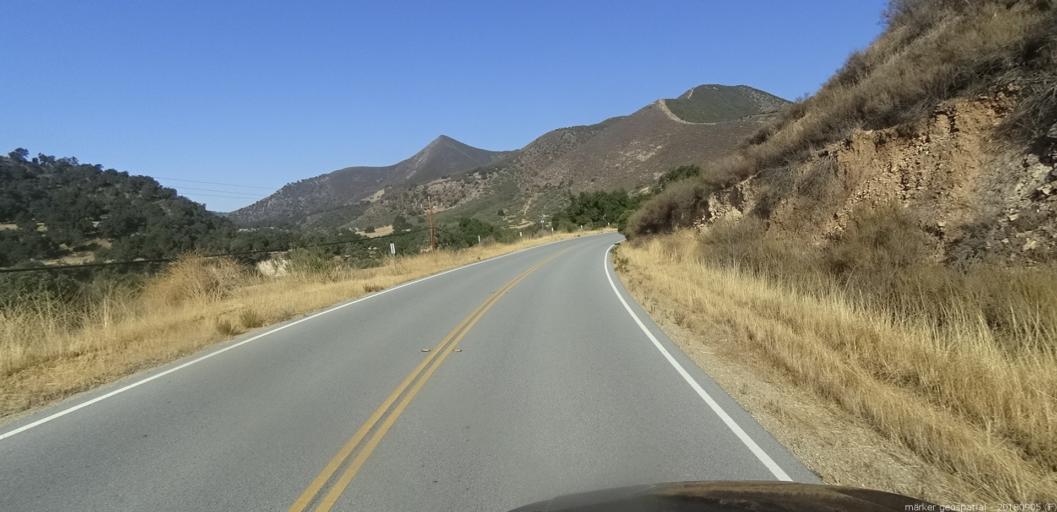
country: US
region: California
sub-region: Monterey County
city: Greenfield
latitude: 36.2402
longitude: -121.4357
